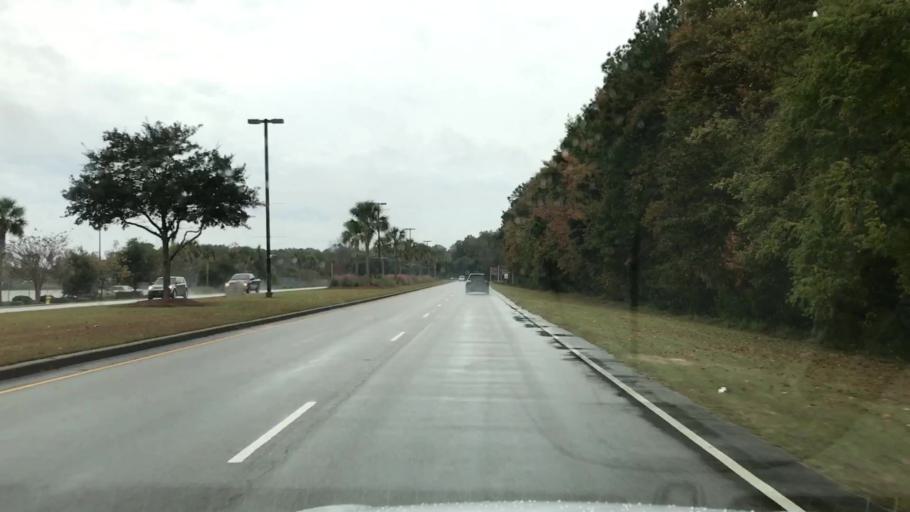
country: US
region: South Carolina
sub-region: Berkeley County
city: Hanahan
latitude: 32.8764
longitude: -80.0376
